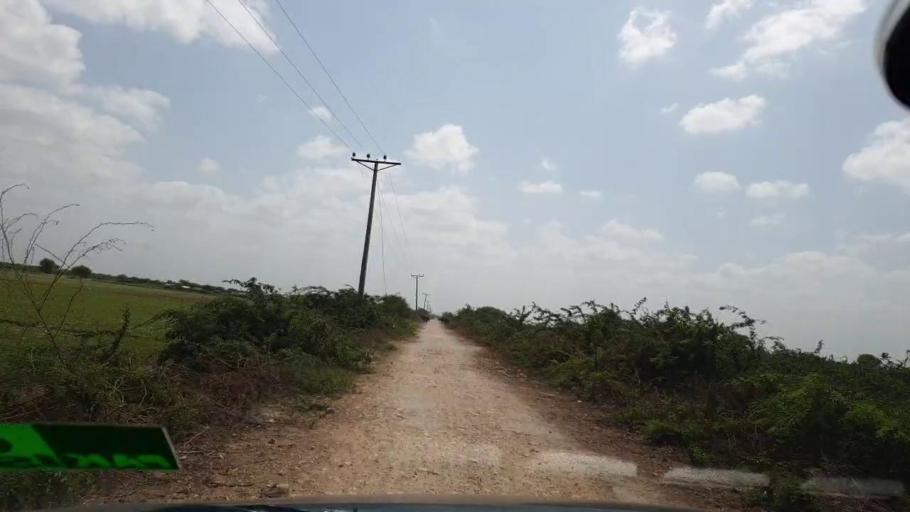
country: PK
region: Sindh
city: Kadhan
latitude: 24.6126
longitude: 69.1853
